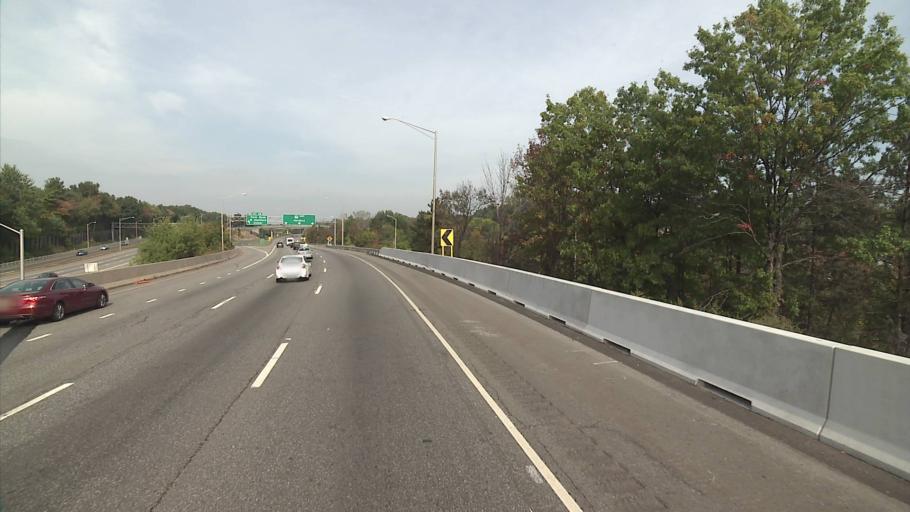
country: US
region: Connecticut
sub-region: Hartford County
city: West Hartford
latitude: 41.7427
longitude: -72.7348
